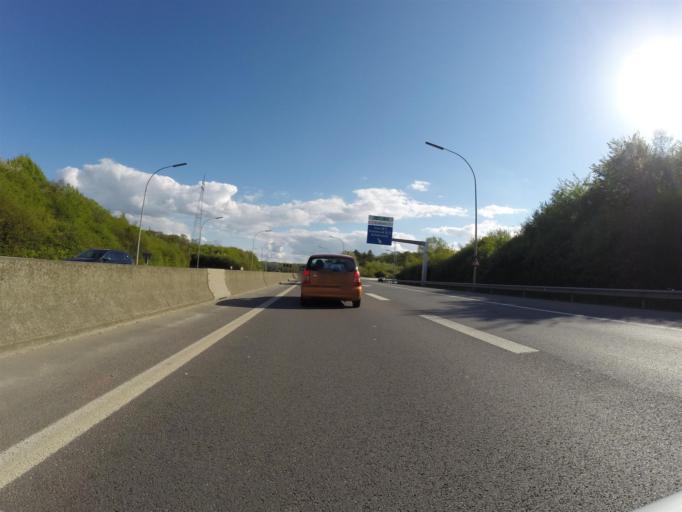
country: LU
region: Luxembourg
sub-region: Canton de Luxembourg
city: Hesperange
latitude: 49.5762
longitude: 6.1245
